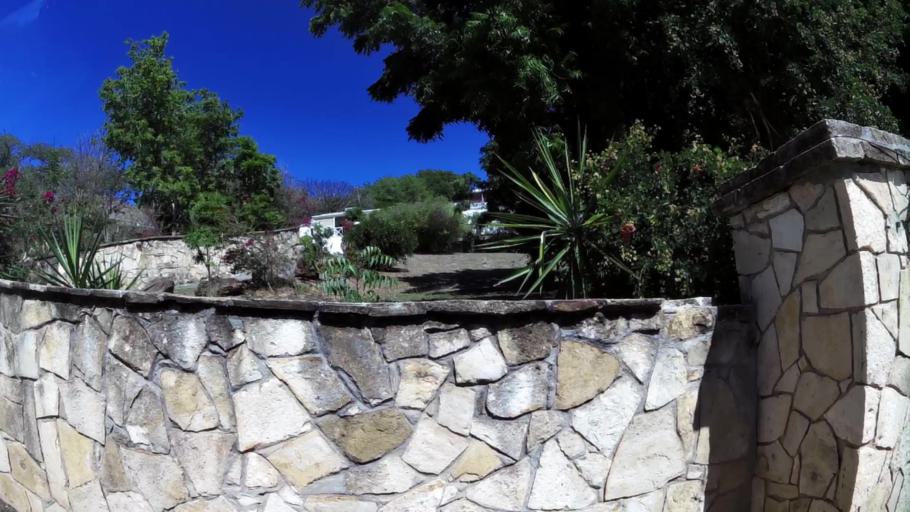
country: AG
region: Saint Paul
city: Falmouth
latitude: 17.0055
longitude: -61.7594
